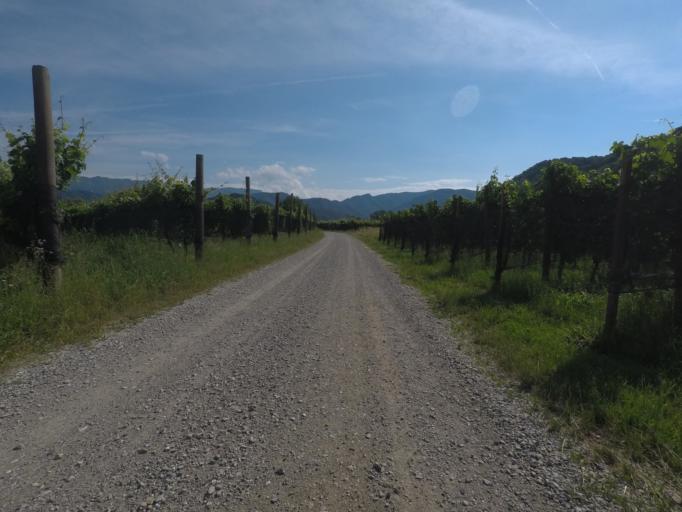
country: IT
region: Friuli Venezia Giulia
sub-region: Provincia di Udine
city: Nimis
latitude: 46.1923
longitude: 13.2655
